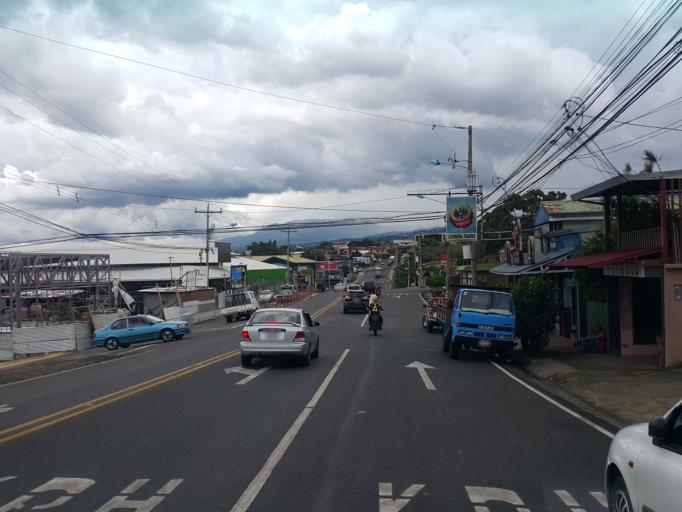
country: CR
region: Heredia
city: Heredia
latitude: 10.0144
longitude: -84.1214
